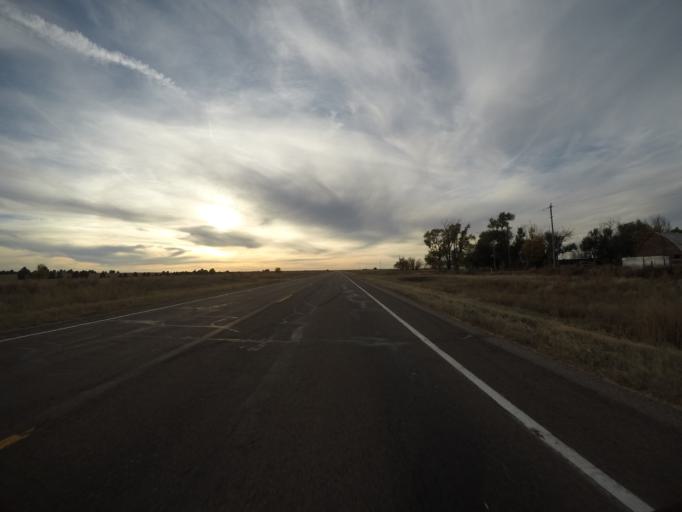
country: US
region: Colorado
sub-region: Yuma County
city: Yuma
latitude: 39.6702
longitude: -102.8857
